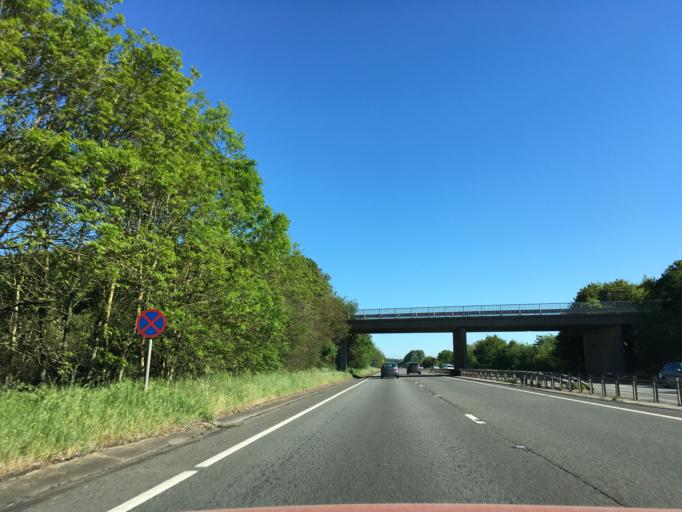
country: GB
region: Wales
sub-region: Monmouthshire
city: Llangwm
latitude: 51.7437
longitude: -2.8418
